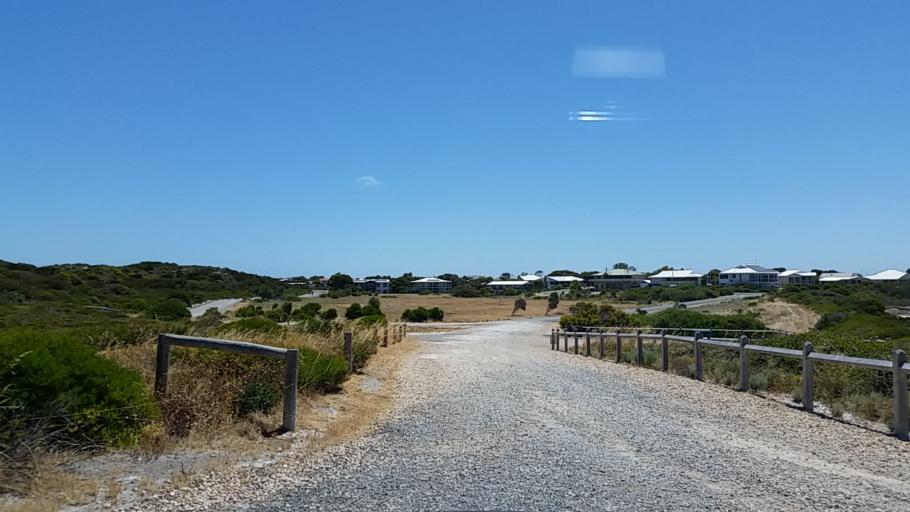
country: AU
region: South Australia
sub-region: Yorke Peninsula
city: Honiton
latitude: -35.2476
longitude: 136.9816
